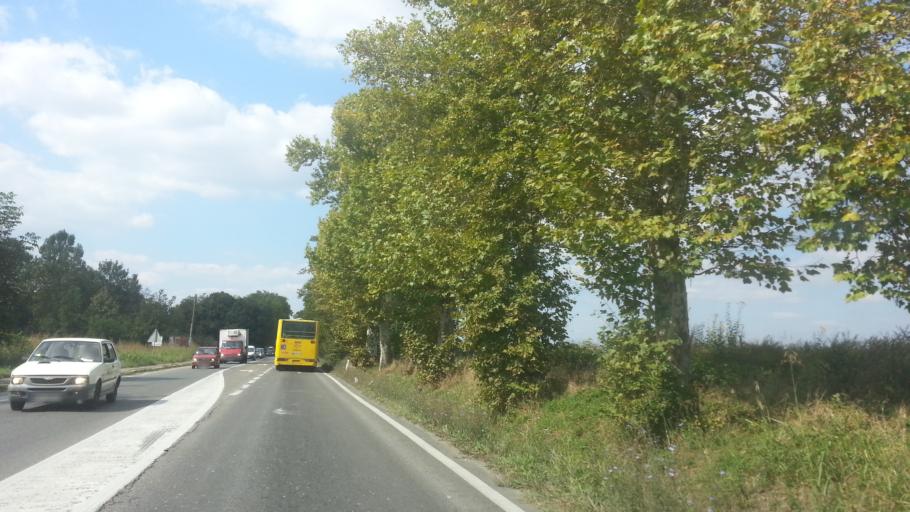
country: RS
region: Central Serbia
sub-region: Belgrade
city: Zemun
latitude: 44.8793
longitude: 20.3314
